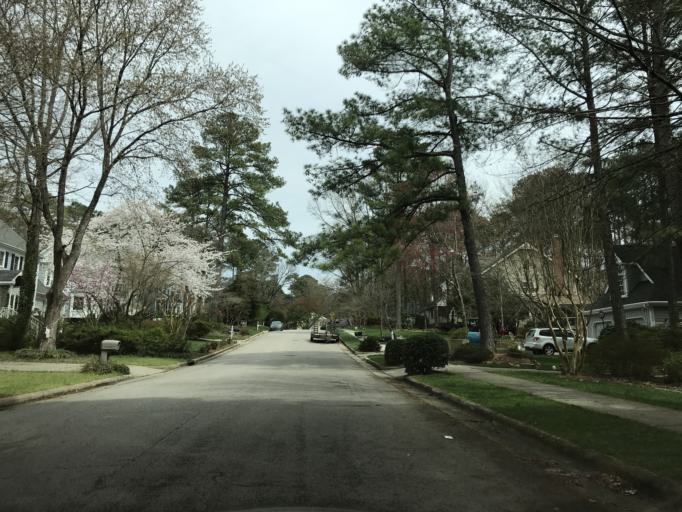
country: US
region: North Carolina
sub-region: Wake County
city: West Raleigh
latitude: 35.8858
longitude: -78.6846
